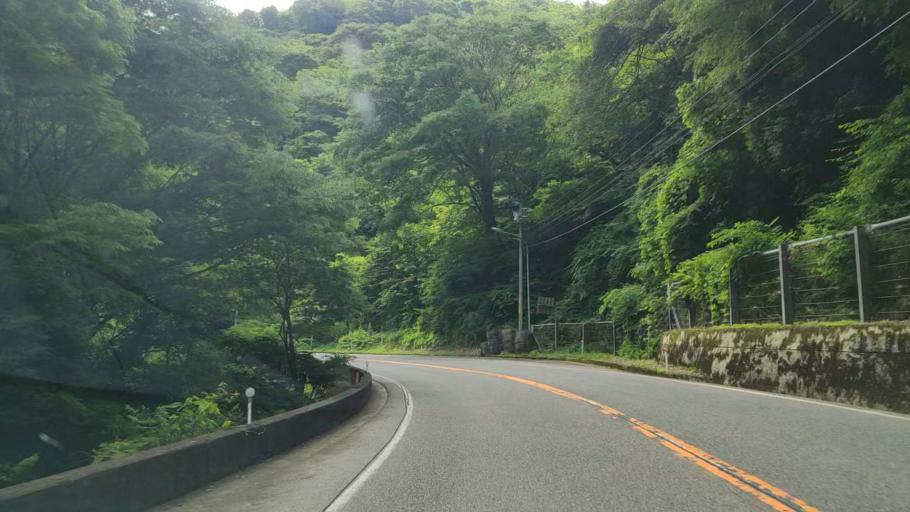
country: JP
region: Okayama
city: Niimi
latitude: 35.2125
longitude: 133.4842
